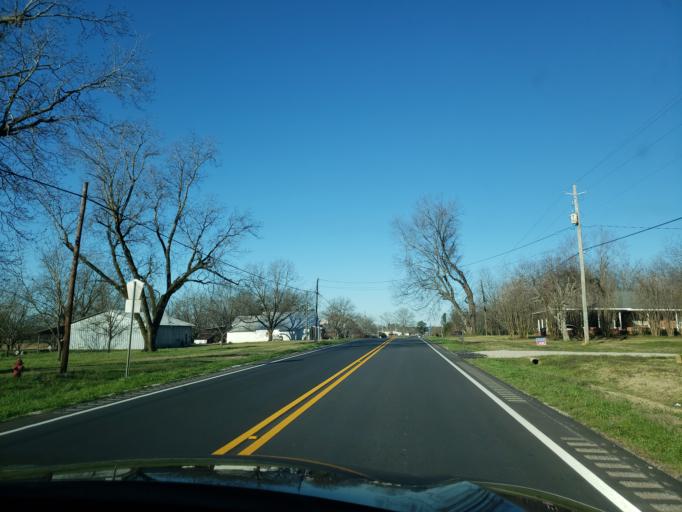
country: US
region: Alabama
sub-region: Elmore County
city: Tallassee
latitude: 32.5822
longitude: -85.7363
